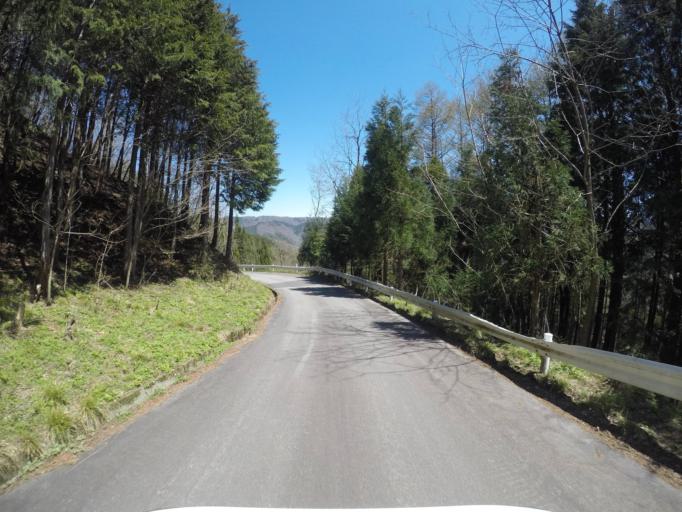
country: JP
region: Gifu
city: Takayama
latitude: 36.1555
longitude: 137.4293
